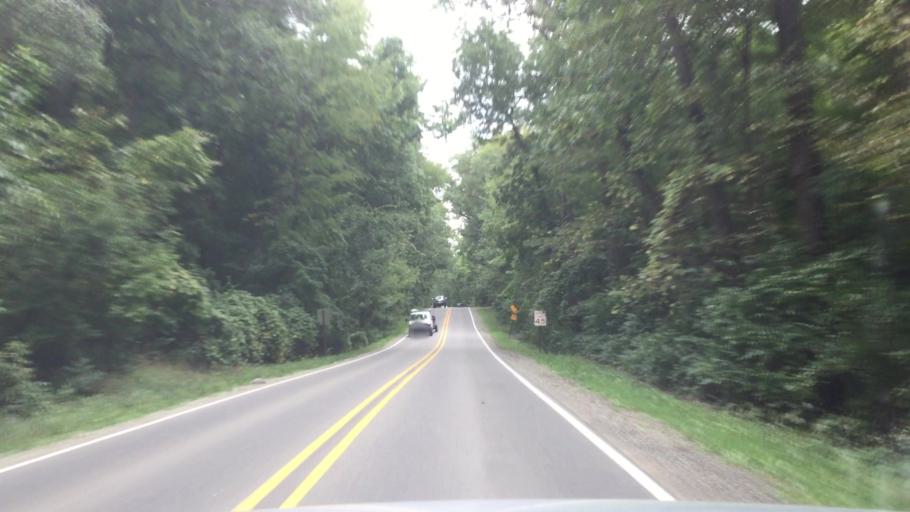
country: US
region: Michigan
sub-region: Livingston County
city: Whitmore Lake
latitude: 42.4620
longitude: -83.7876
